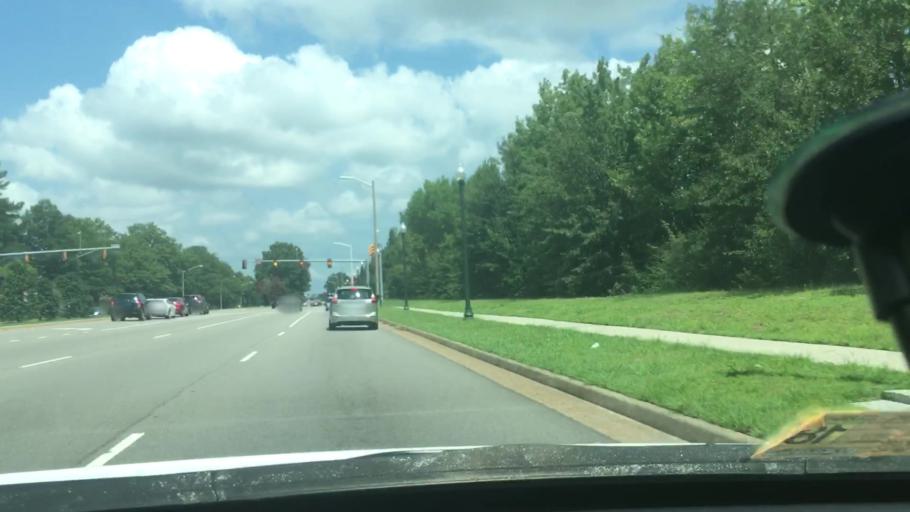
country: US
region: Virginia
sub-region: City of Chesapeake
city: Chesapeake
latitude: 36.7707
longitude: -76.2281
